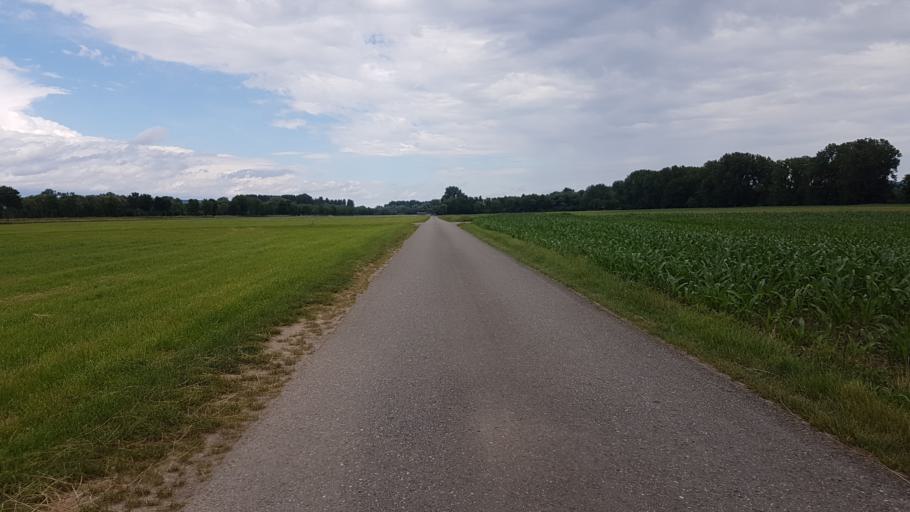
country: DE
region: Baden-Wuerttemberg
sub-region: Tuebingen Region
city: Neufra
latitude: 48.1218
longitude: 9.4566
